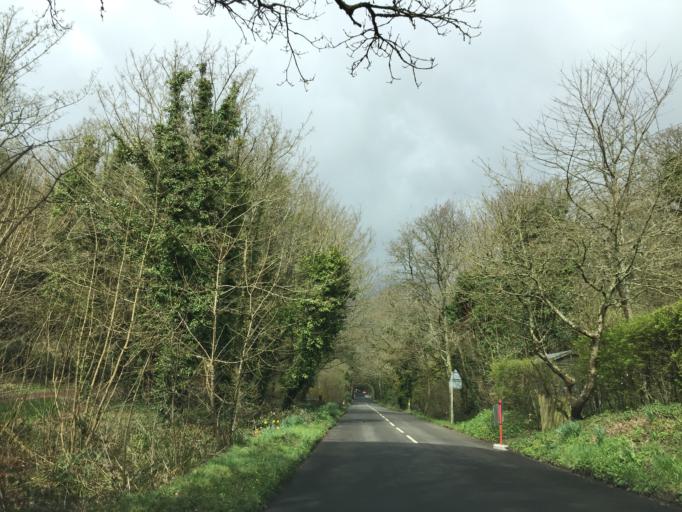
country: JE
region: St Helier
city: Saint Helier
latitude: 49.2153
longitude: -2.1716
